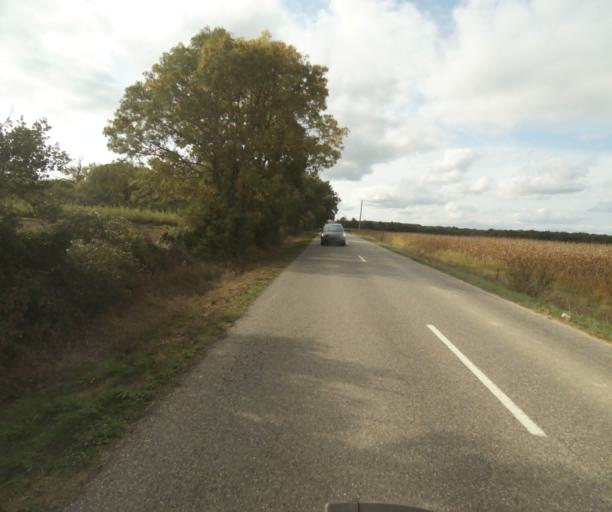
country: FR
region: Midi-Pyrenees
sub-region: Departement du Tarn-et-Garonne
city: Verdun-sur-Garonne
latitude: 43.8489
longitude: 1.1449
